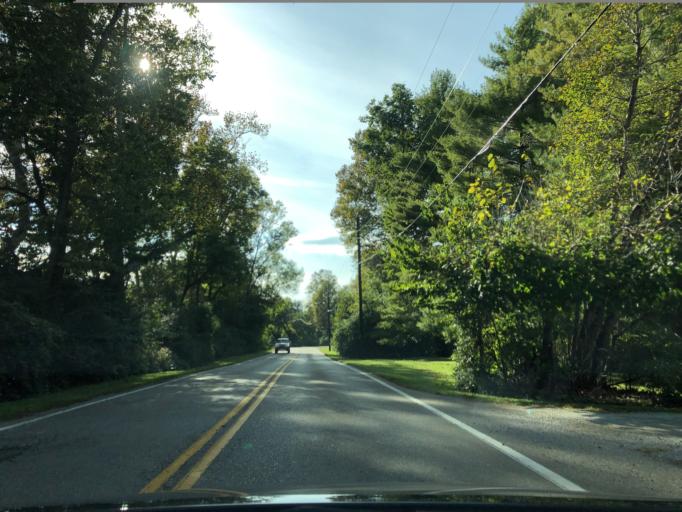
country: US
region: Ohio
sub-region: Hamilton County
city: The Village of Indian Hill
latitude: 39.2513
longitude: -84.2877
